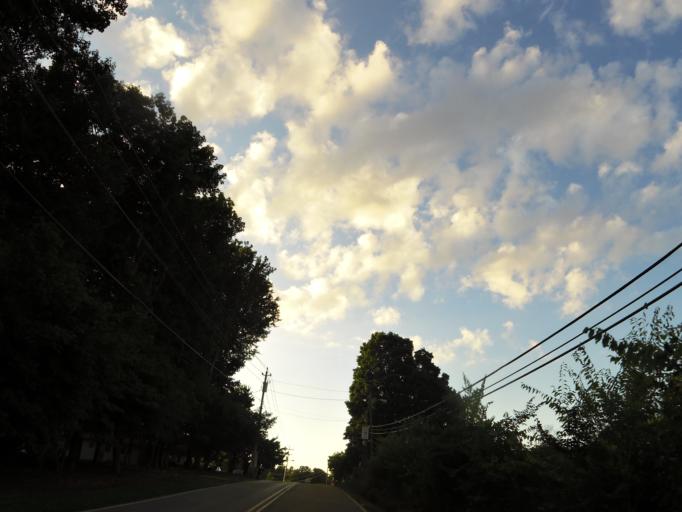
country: US
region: Tennessee
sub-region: Knox County
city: Farragut
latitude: 35.9059
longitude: -84.1698
